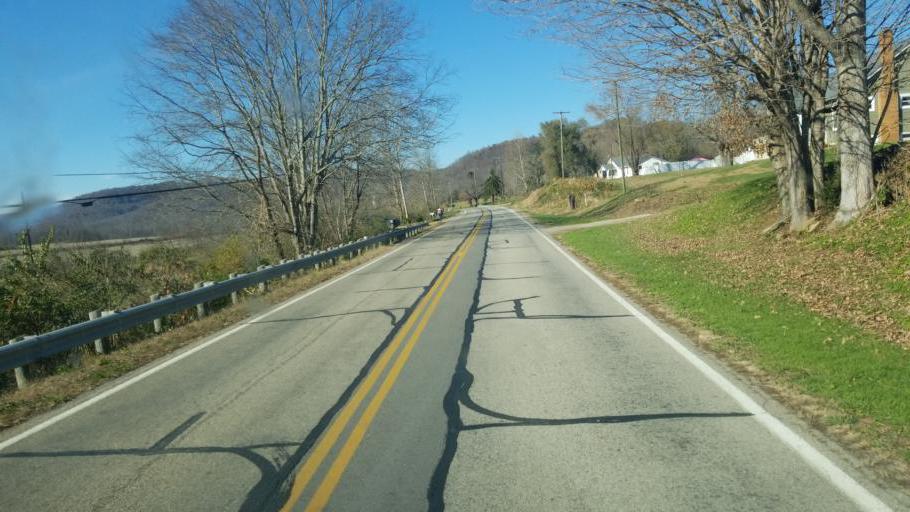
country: US
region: Kentucky
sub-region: Lewis County
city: Vanceburg
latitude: 38.6333
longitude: -83.2138
